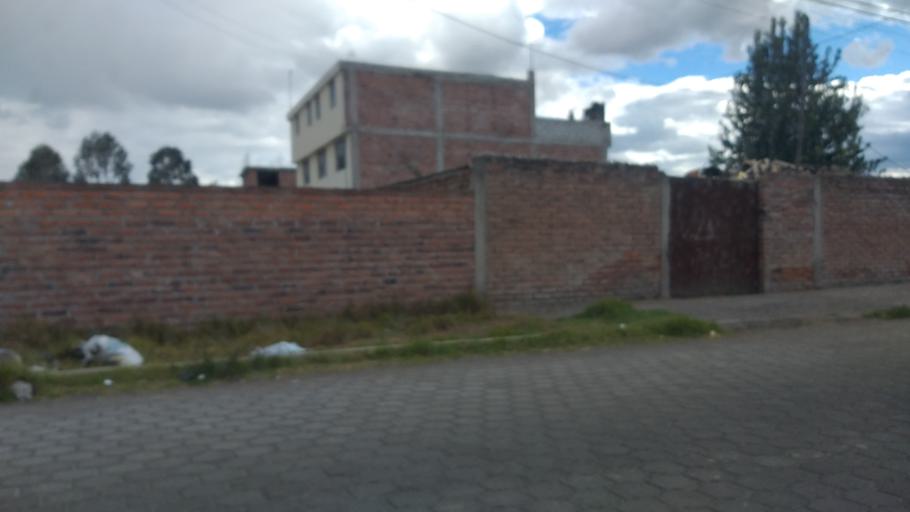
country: EC
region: Chimborazo
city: Riobamba
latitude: -1.6875
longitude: -78.6283
